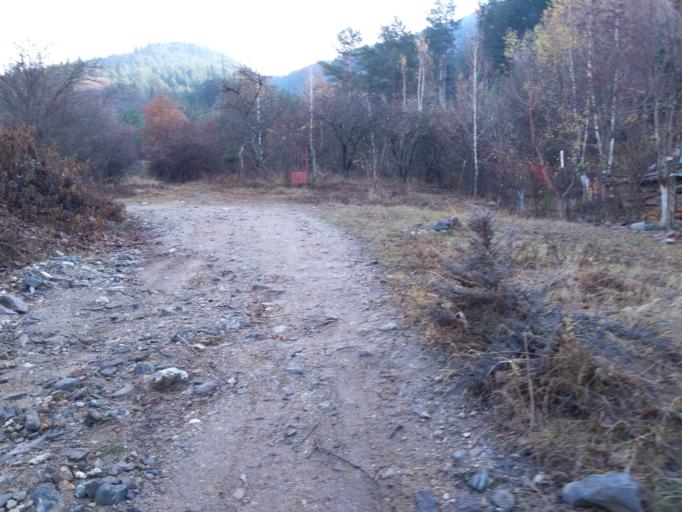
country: BG
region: Kyustendil
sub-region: Obshtina Dupnitsa
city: Dupnitsa
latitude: 42.2403
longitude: 23.1744
